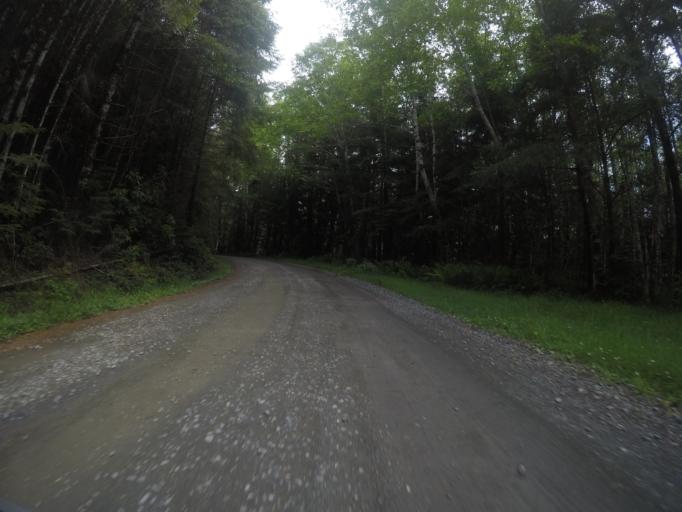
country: US
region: California
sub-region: Humboldt County
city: Westhaven-Moonstone
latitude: 41.2236
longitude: -124.0033
